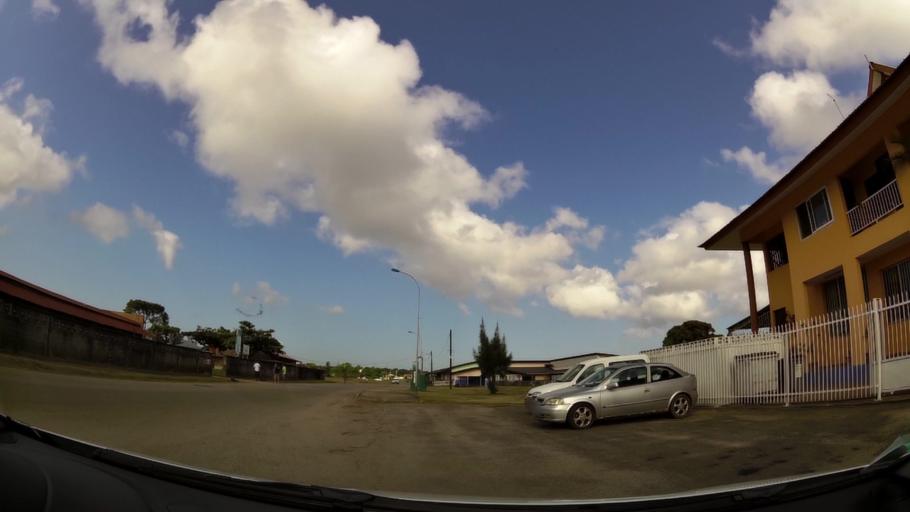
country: GF
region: Guyane
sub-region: Guyane
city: Cayenne
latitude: 4.9313
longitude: -52.3206
